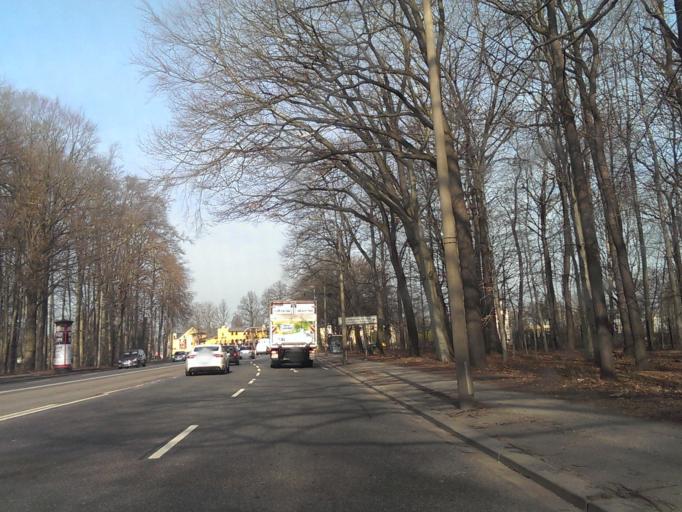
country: DE
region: Saxony
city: Chemnitz
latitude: 50.8497
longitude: 12.8949
